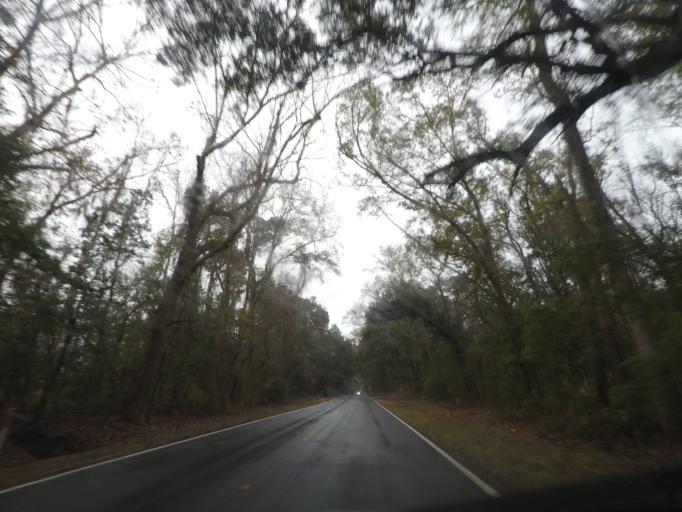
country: US
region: South Carolina
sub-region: Charleston County
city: Meggett
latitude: 32.6922
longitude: -80.3496
